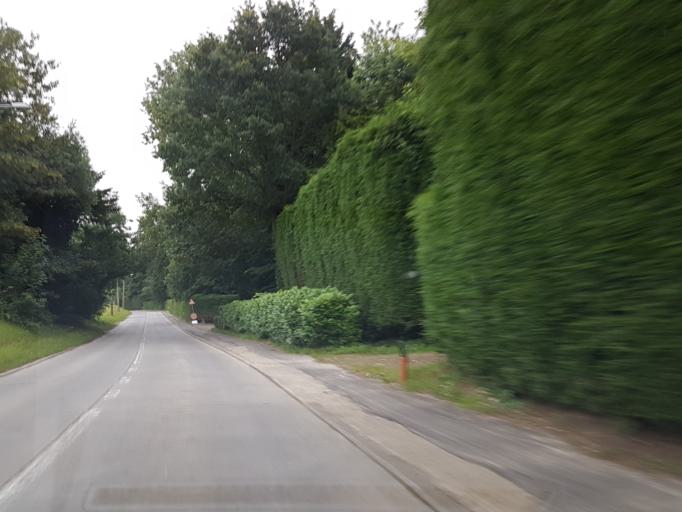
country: BE
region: Flanders
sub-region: Provincie Vlaams-Brabant
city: Wemmel
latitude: 50.9363
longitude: 4.2801
